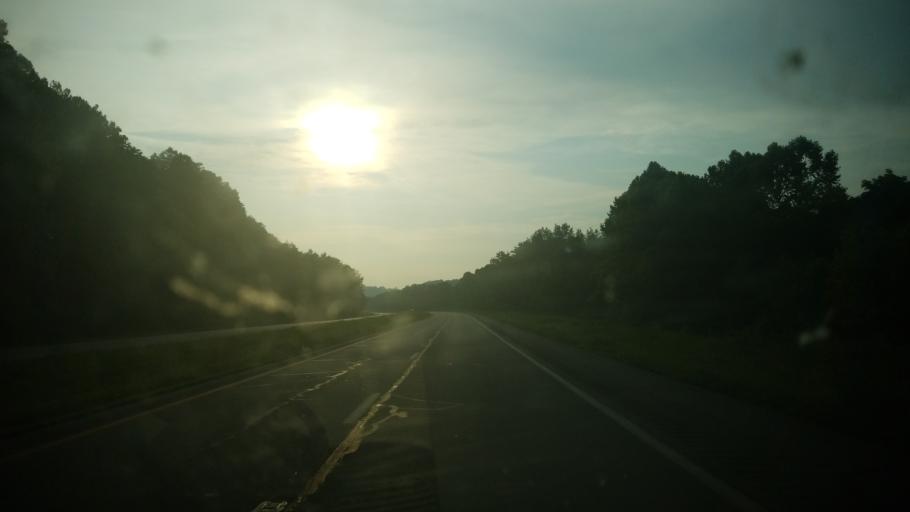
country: US
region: Ohio
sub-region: Pike County
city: Piketon
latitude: 39.0585
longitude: -83.0707
